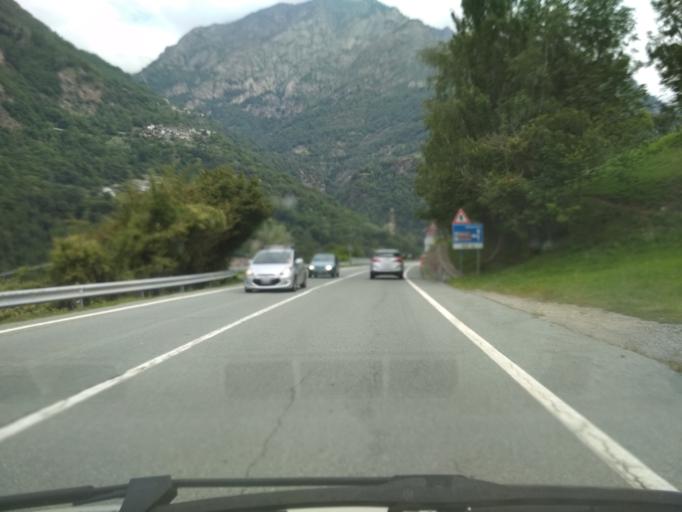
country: IT
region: Aosta Valley
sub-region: Valle d'Aosta
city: Perloz
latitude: 45.6146
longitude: 7.8147
